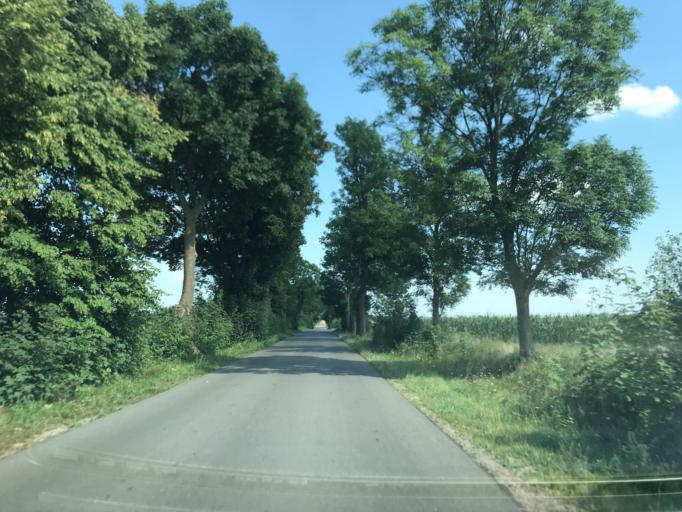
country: PL
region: Masovian Voivodeship
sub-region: Powiat zurominski
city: Lubowidz
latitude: 53.1741
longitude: 19.8757
